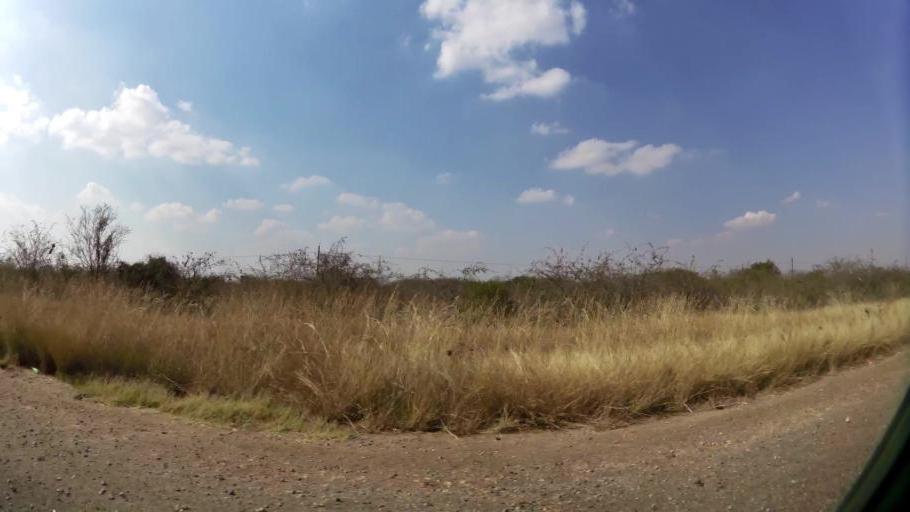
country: ZA
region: North-West
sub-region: Bojanala Platinum District Municipality
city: Rustenburg
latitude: -25.5130
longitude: 27.1004
